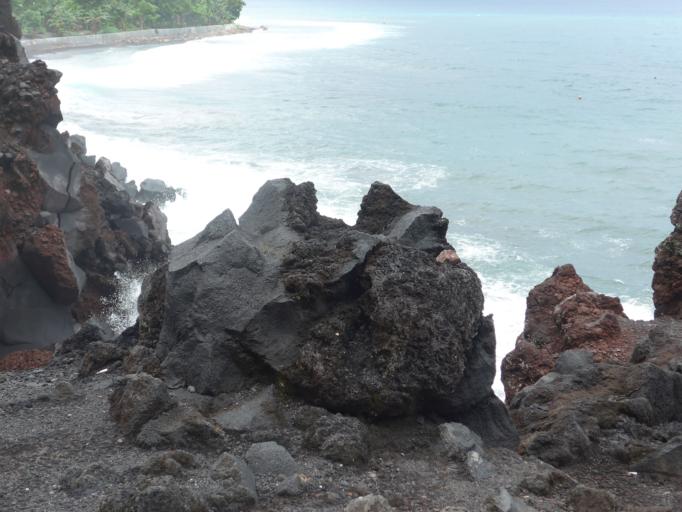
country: ID
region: Maluku Utara
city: Ternate
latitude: 0.8463
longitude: 127.3661
